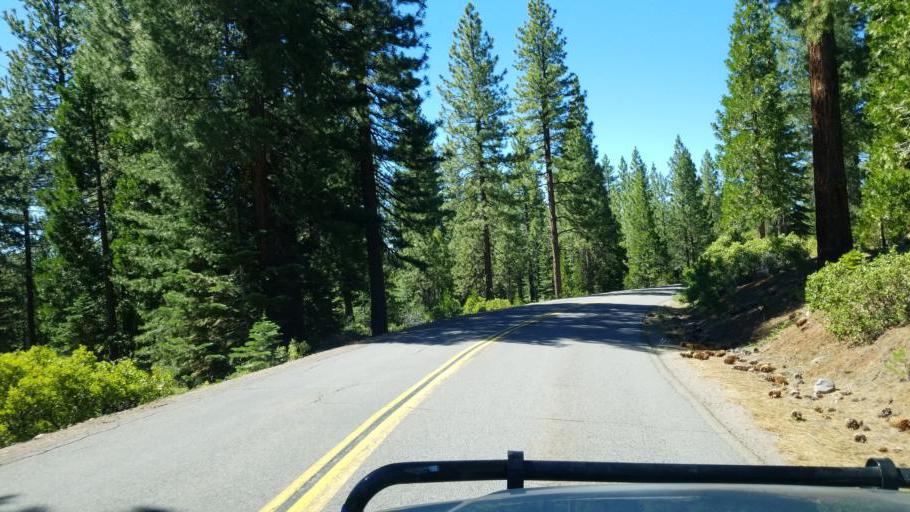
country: US
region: California
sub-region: Lassen County
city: Susanville
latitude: 40.4581
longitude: -120.7606
